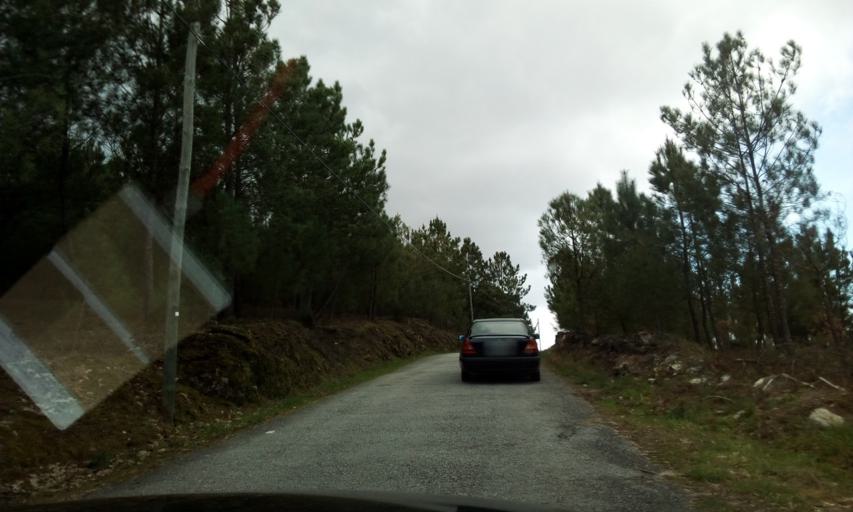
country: PT
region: Guarda
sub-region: Fornos de Algodres
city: Fornos de Algodres
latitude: 40.6366
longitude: -7.5774
